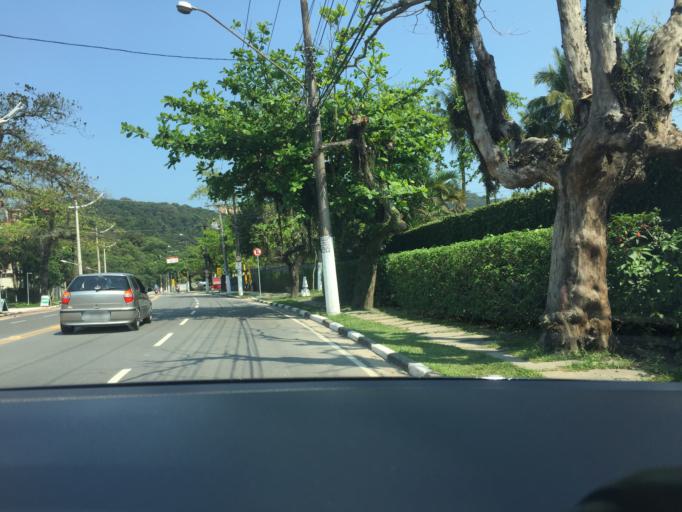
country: BR
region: Sao Paulo
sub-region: Guaruja
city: Guaruja
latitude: -23.9732
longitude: -46.1892
